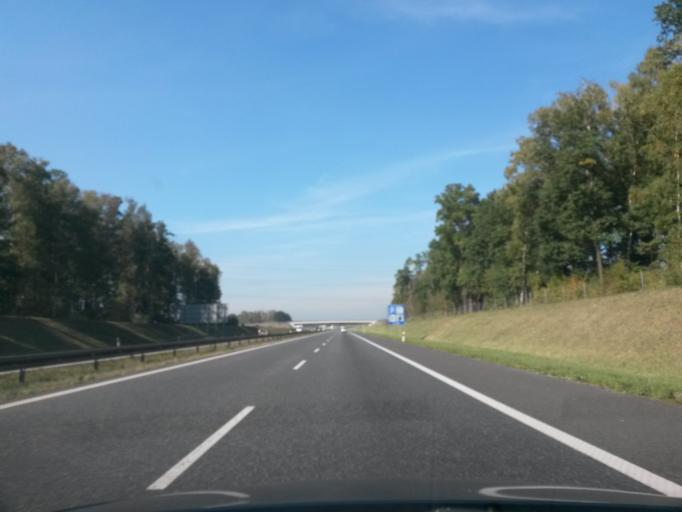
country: PL
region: Silesian Voivodeship
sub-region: Powiat gliwicki
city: Sosnicowice
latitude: 50.2889
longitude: 18.5644
